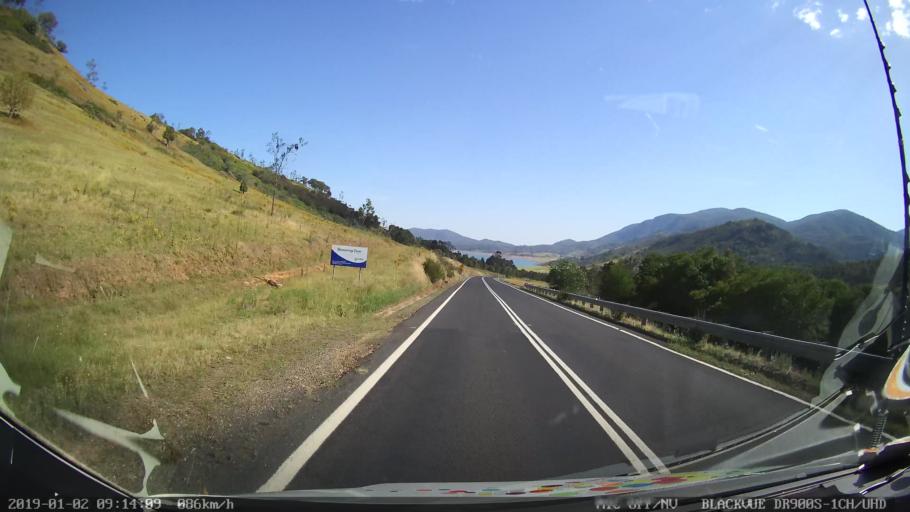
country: AU
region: New South Wales
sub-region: Tumut Shire
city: Tumut
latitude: -35.4808
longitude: 148.2726
